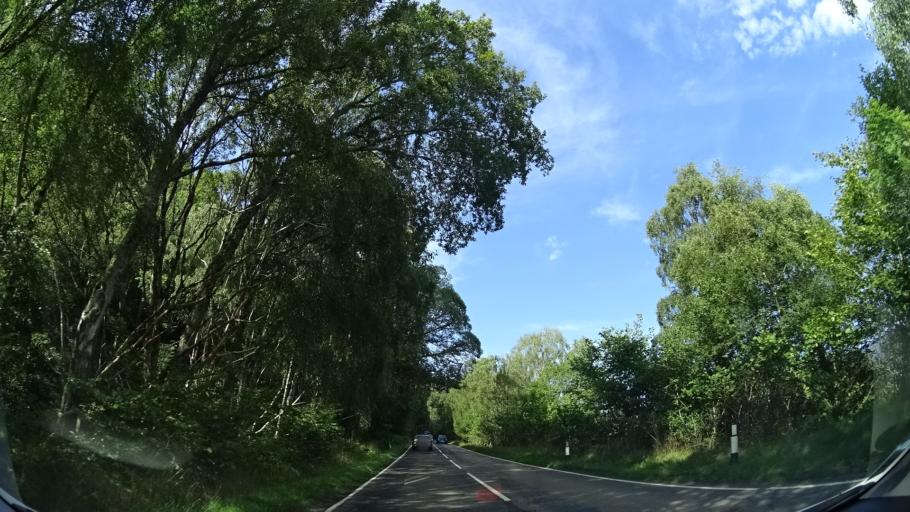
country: GB
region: Scotland
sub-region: Highland
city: Beauly
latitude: 57.2949
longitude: -4.4737
